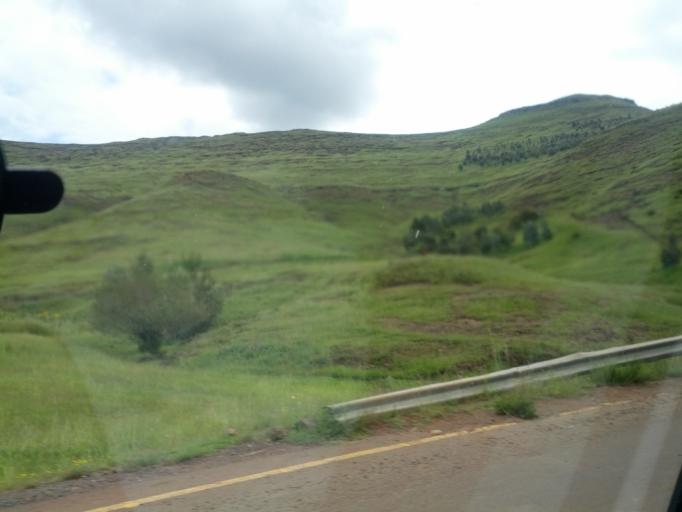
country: LS
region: Leribe
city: Leribe
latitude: -29.0350
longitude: 28.2362
